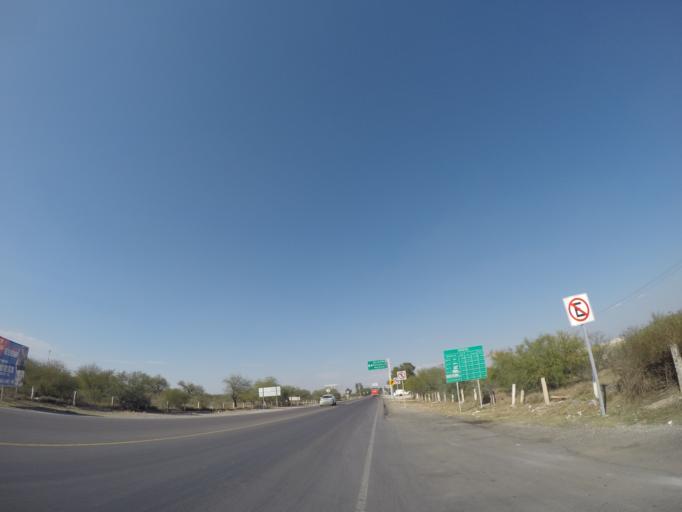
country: MX
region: San Luis Potosi
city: Rio Verde
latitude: 21.9223
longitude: -99.9596
